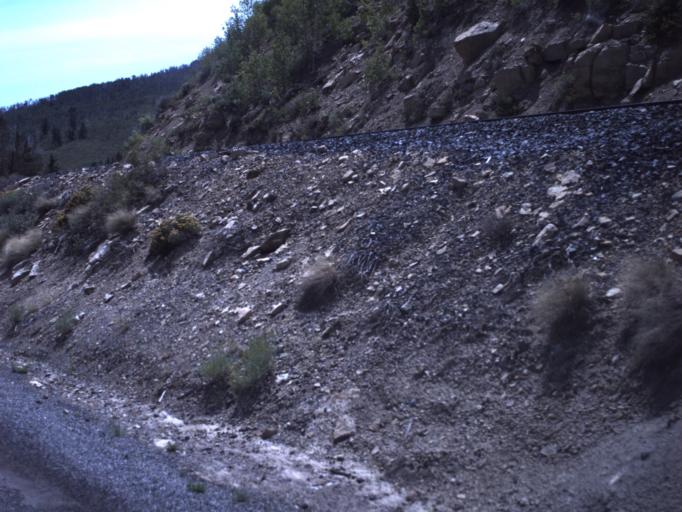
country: US
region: Utah
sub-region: Carbon County
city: Helper
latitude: 39.7864
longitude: -111.1214
